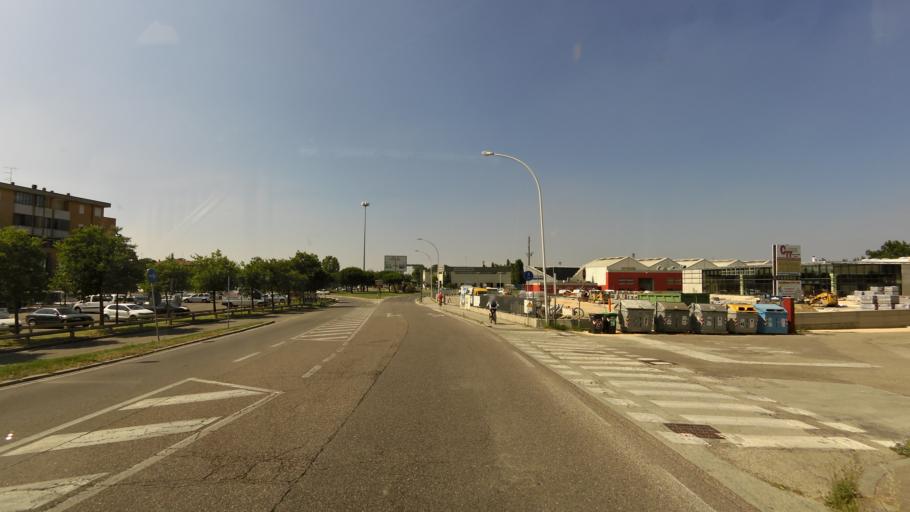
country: IT
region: Emilia-Romagna
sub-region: Provincia di Ravenna
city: Ravenna
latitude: 44.3995
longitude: 12.2149
